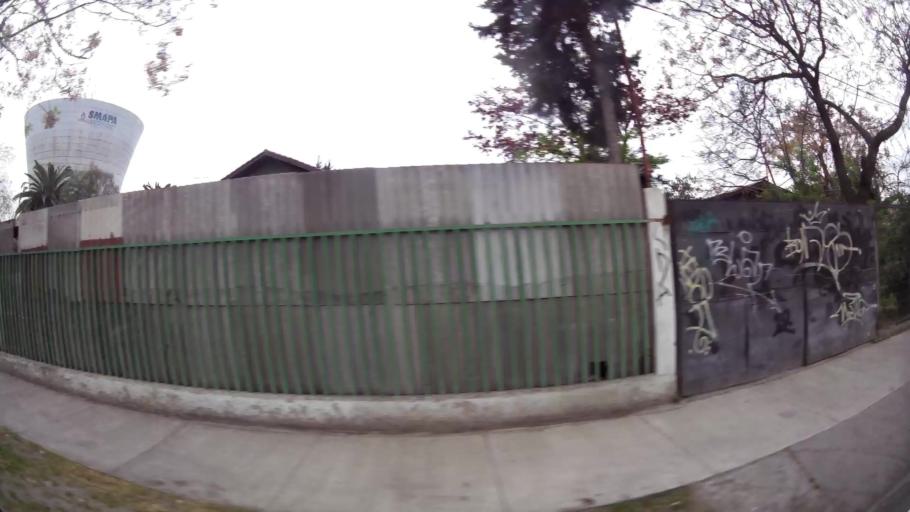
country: CL
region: Santiago Metropolitan
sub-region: Provincia de Santiago
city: Lo Prado
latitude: -33.5070
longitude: -70.7629
